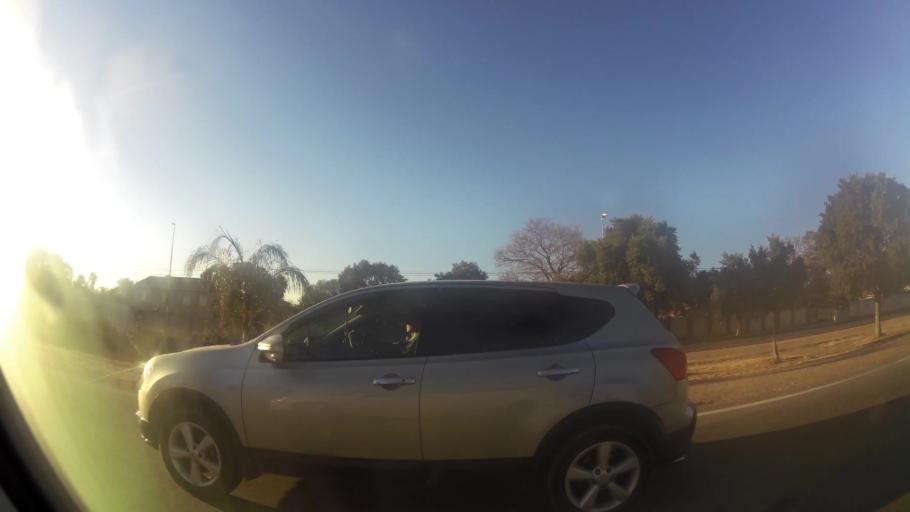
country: ZA
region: Limpopo
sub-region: Capricorn District Municipality
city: Polokwane
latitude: -23.9183
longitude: 29.4408
